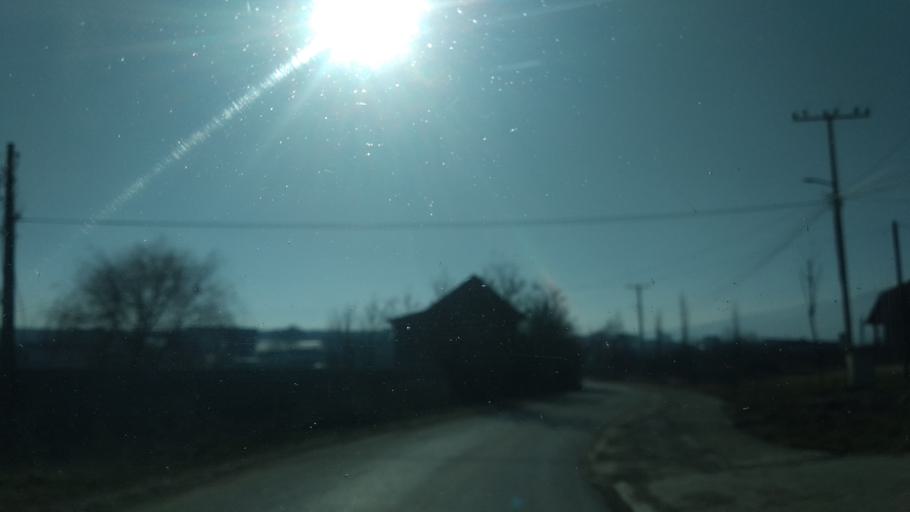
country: XK
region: Pristina
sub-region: Komuna e Gracanices
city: Glanica
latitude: 42.6051
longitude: 21.0284
